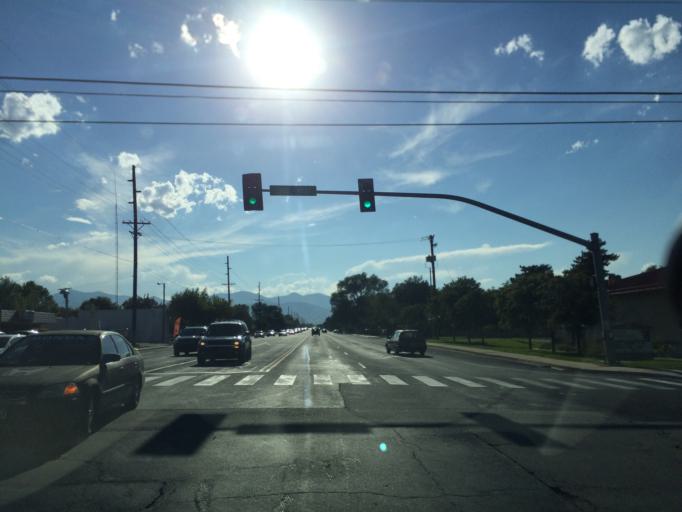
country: US
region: Utah
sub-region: Salt Lake County
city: Taylorsville
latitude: 40.6822
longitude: -111.9673
